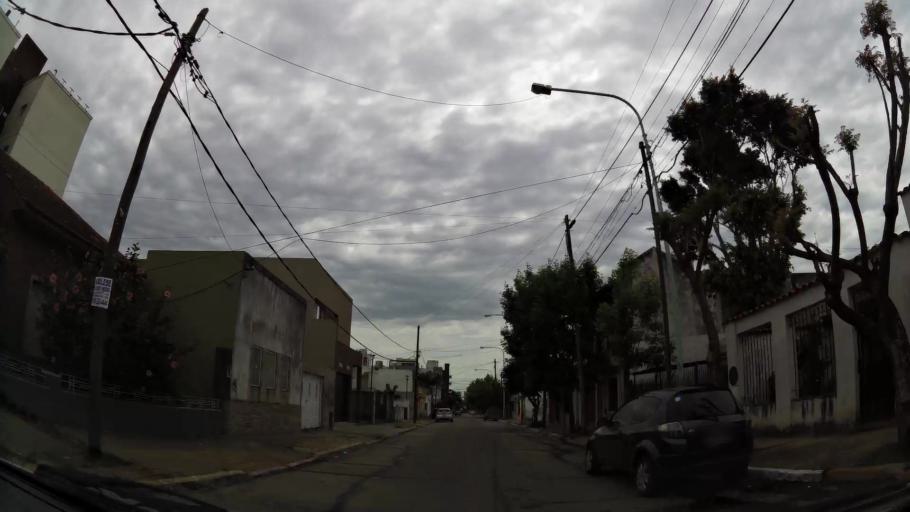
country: AR
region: Buenos Aires
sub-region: Partido de Quilmes
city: Quilmes
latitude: -34.7643
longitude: -58.2040
